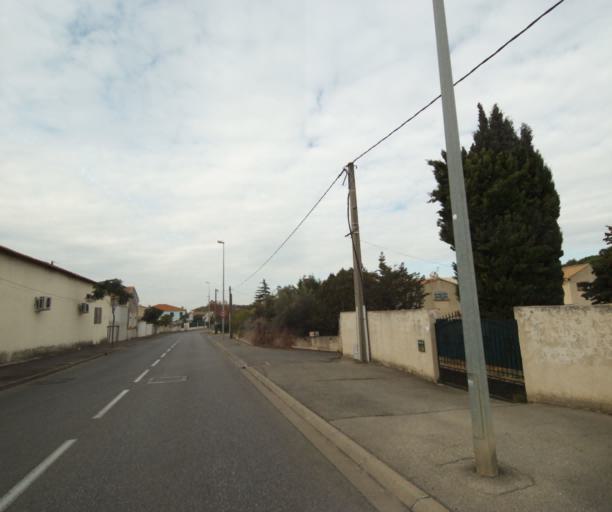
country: FR
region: Provence-Alpes-Cote d'Azur
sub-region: Departement des Bouches-du-Rhone
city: Saint-Victoret
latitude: 43.4196
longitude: 5.2399
